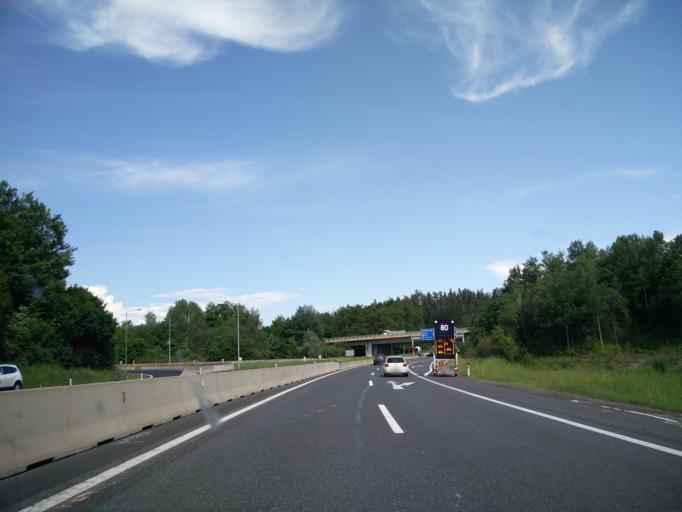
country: AT
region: Carinthia
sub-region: Klagenfurt am Woerthersee
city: Klagenfurt am Woerthersee
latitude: 46.6597
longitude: 14.2895
